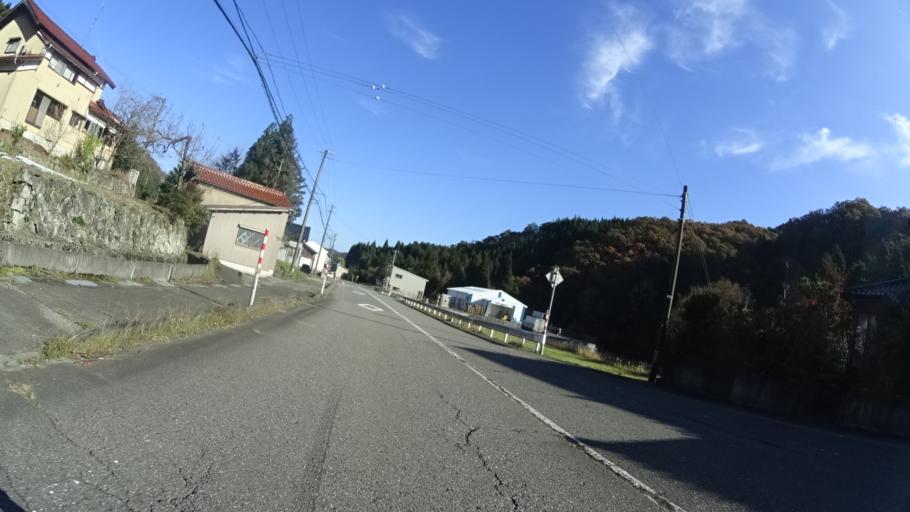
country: JP
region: Ishikawa
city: Komatsu
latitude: 36.2564
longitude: 136.3923
